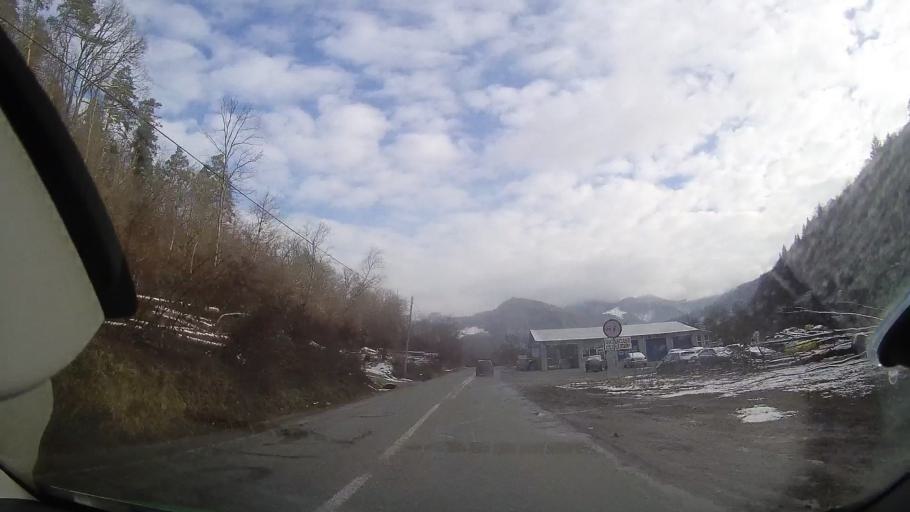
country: RO
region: Alba
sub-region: Oras Baia de Aries
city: Baia de Aries
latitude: 46.3810
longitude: 23.2675
